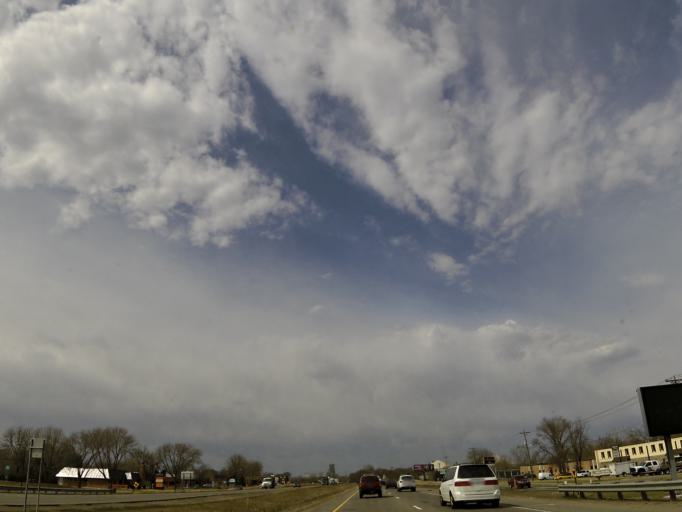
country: US
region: Minnesota
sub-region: Scott County
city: Savage
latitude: 44.7779
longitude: -93.3270
